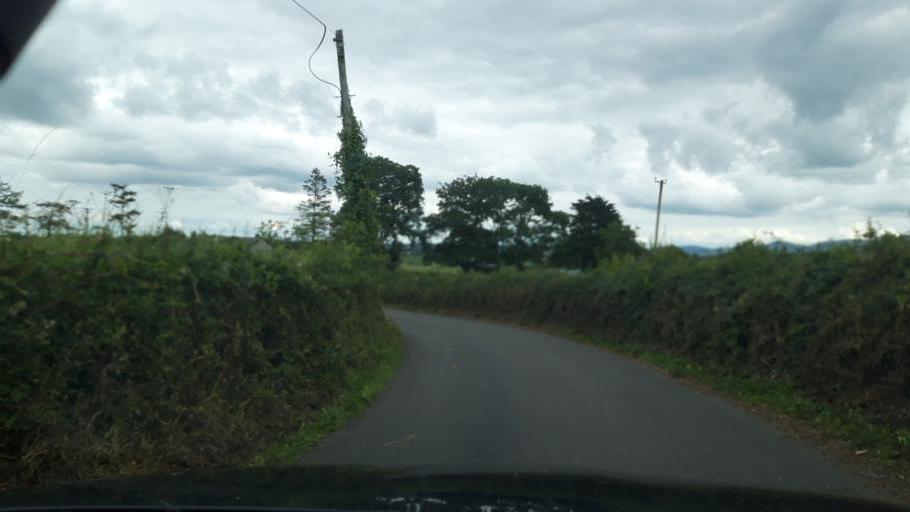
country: IE
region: Leinster
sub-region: Kilkenny
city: Graiguenamanagh
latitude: 52.6057
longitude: -7.0221
